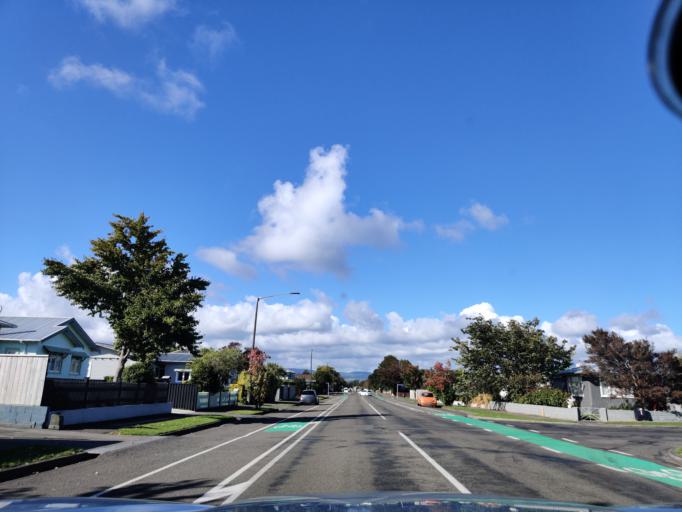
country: NZ
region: Manawatu-Wanganui
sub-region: Palmerston North City
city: Palmerston North
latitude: -40.3483
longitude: 175.5961
